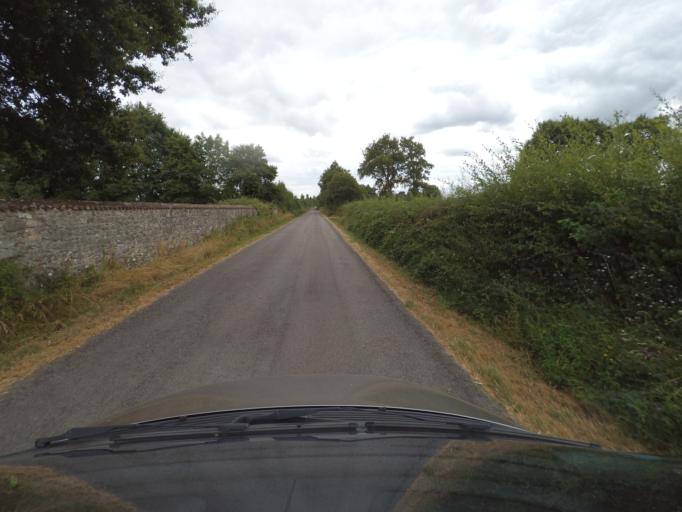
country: FR
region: Limousin
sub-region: Departement de la Haute-Vienne
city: Magnac-Laval
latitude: 46.2918
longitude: 1.2449
